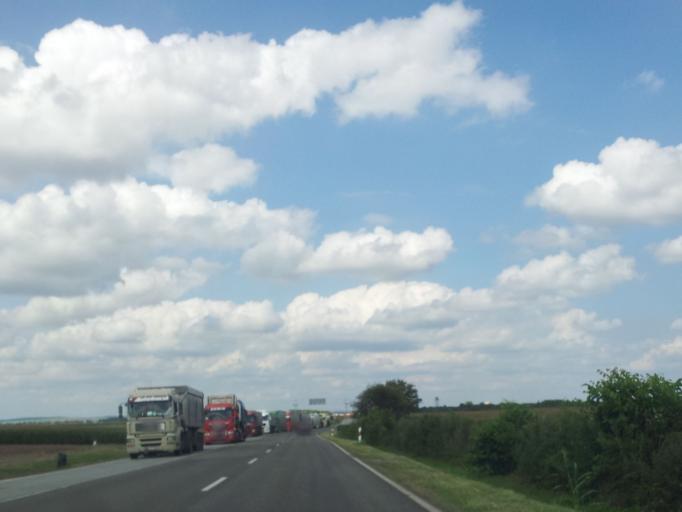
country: HU
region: Baranya
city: Mohacs
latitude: 45.9083
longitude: 18.6595
